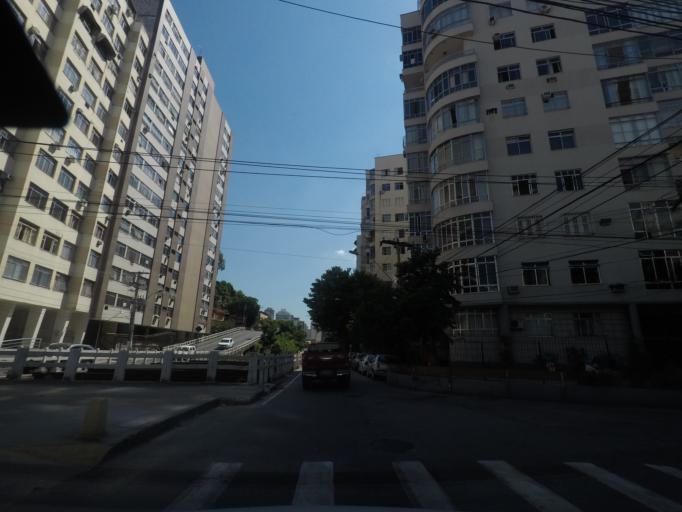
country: BR
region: Rio de Janeiro
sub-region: Niteroi
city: Niteroi
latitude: -22.9113
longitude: -43.1066
